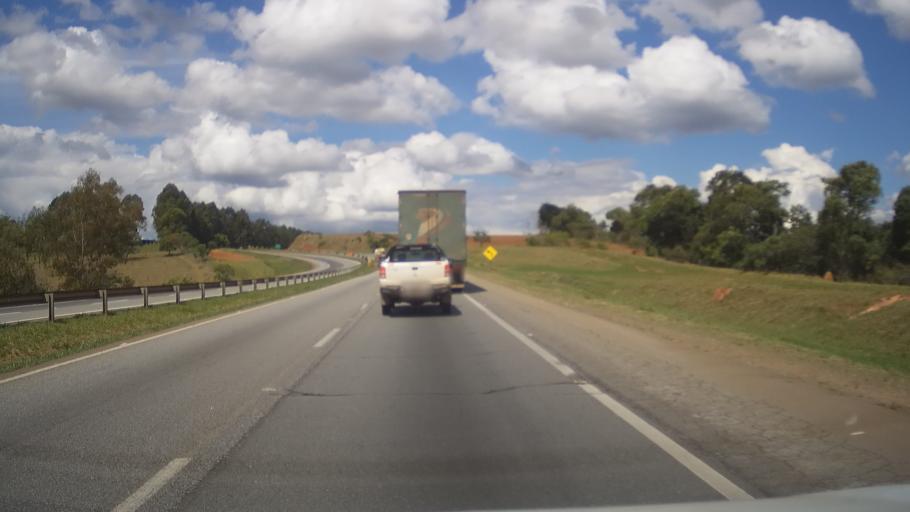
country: BR
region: Minas Gerais
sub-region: Oliveira
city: Oliveira
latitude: -20.8309
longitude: -44.8212
